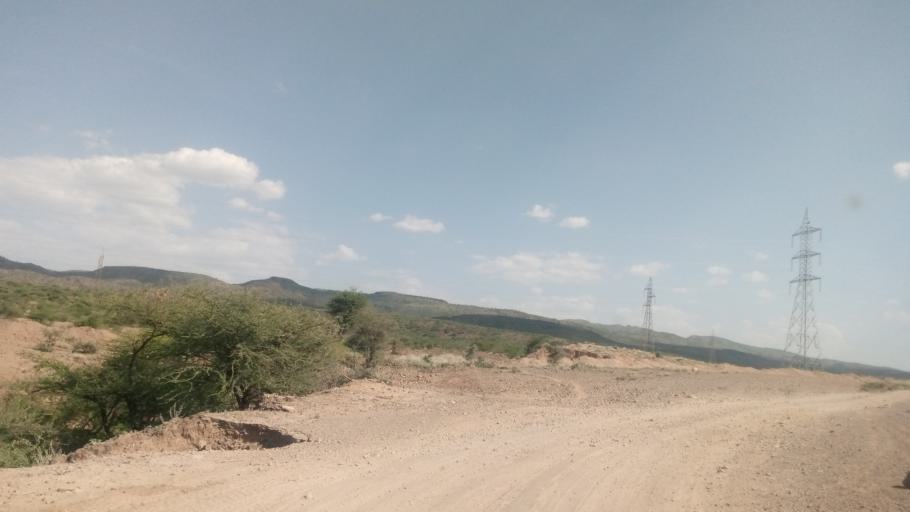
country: ET
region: Oromiya
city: Hirna
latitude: 9.5459
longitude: 41.1524
